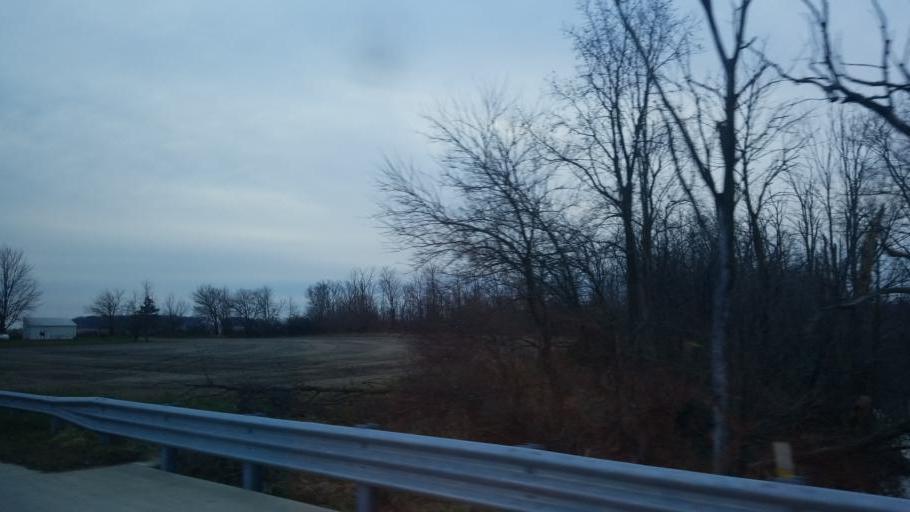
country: US
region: Indiana
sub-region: Adams County
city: Decatur
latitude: 40.7692
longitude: -84.8799
